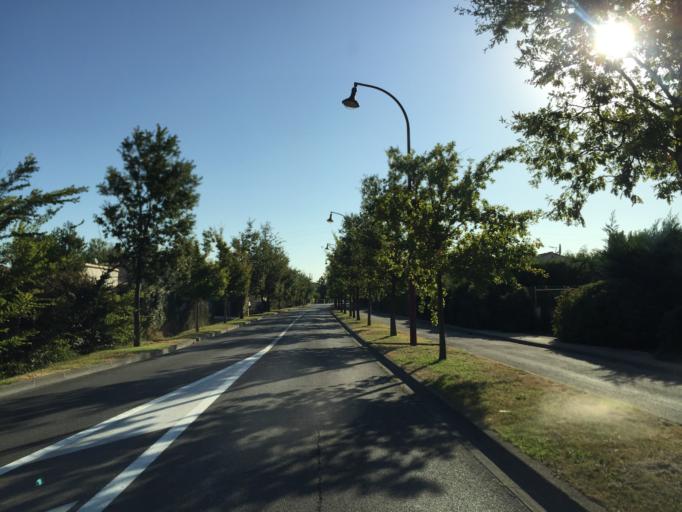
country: FR
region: Provence-Alpes-Cote d'Azur
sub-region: Departement du Vaucluse
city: Entraigues-sur-la-Sorgue
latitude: 44.0035
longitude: 4.9116
